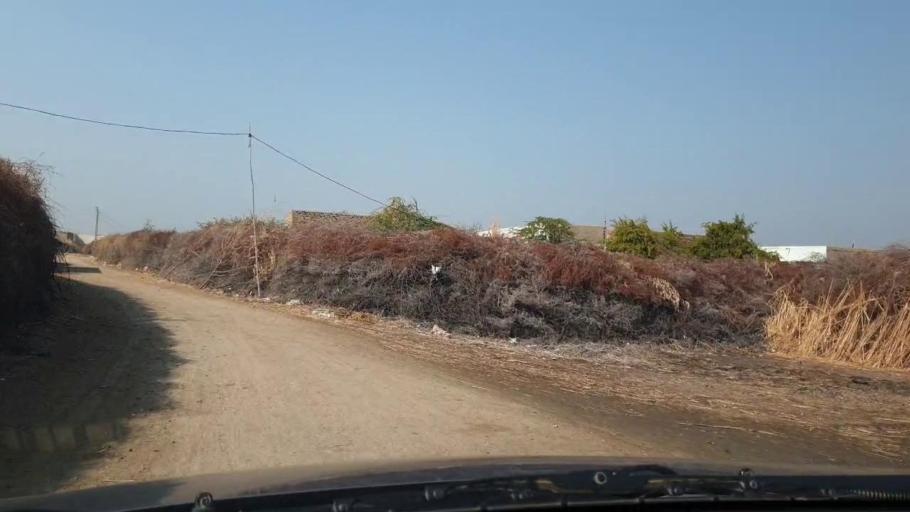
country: PK
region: Sindh
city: Jhol
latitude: 25.9045
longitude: 68.9993
